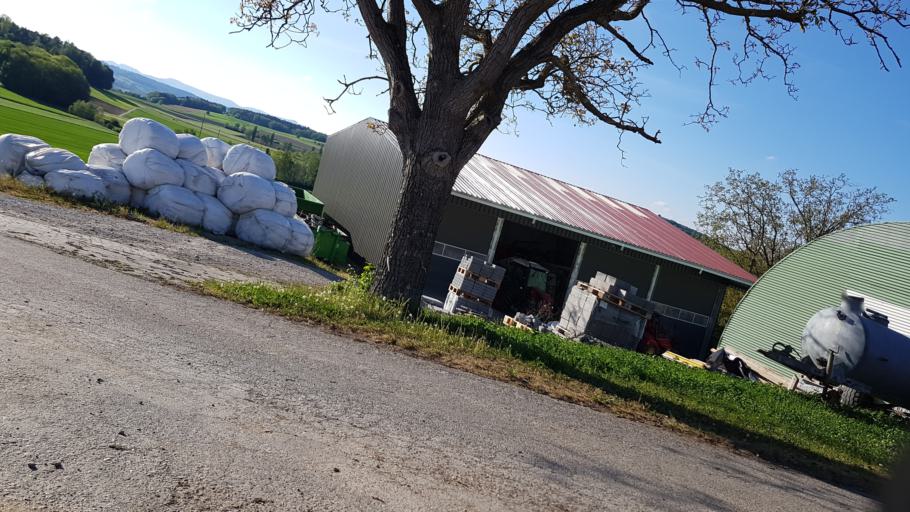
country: CH
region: Aargau
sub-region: Bezirk Bremgarten
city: Sarmenstorf
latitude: 47.3016
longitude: 8.2497
